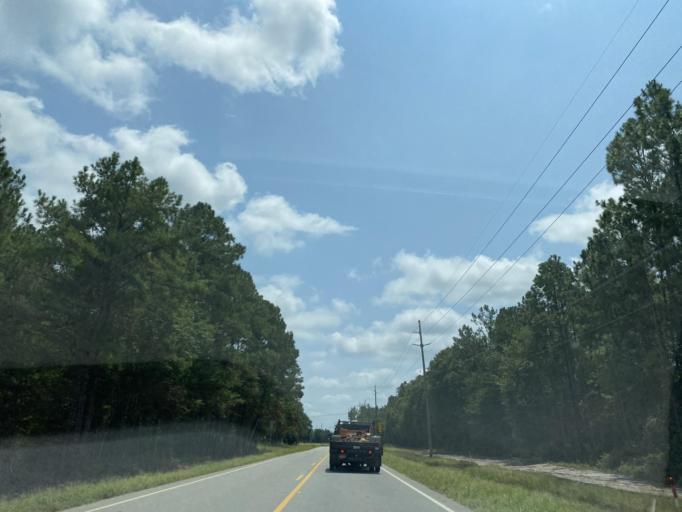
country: US
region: Georgia
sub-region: Jeff Davis County
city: Hazlehurst
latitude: 31.8159
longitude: -82.5677
